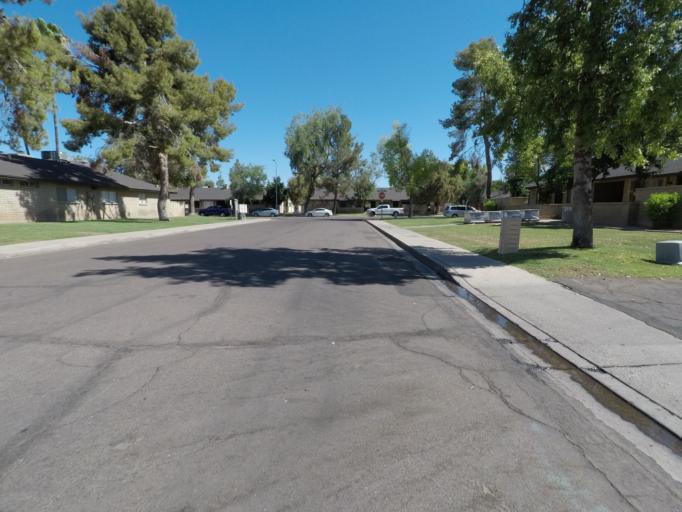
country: US
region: Arizona
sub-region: Maricopa County
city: Tempe Junction
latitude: 33.4016
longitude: -111.9405
